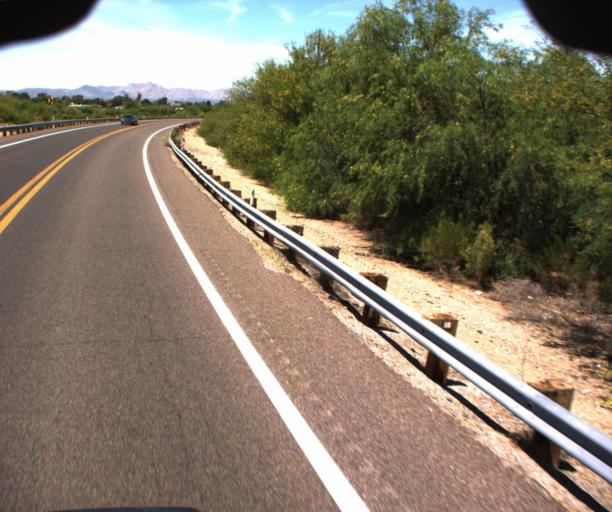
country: US
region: Arizona
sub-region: La Paz County
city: Salome
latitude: 33.8233
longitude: -113.5297
